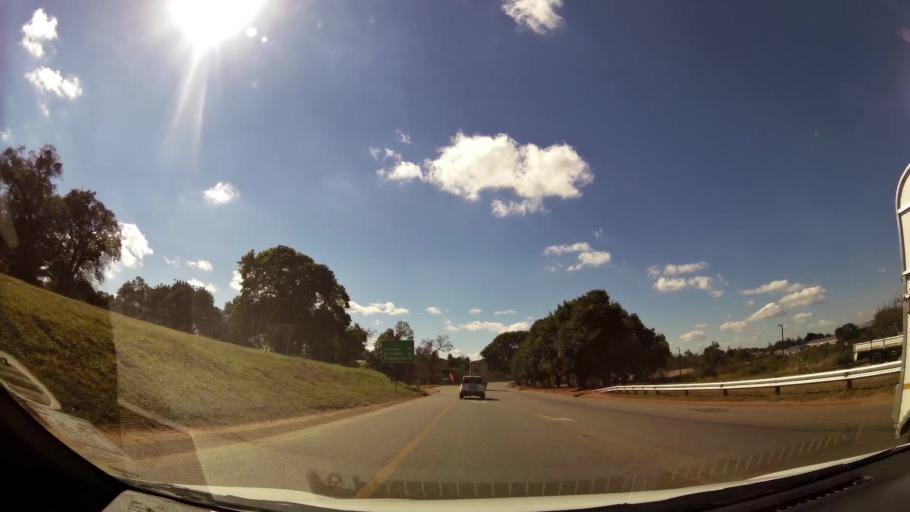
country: ZA
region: Limpopo
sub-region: Mopani District Municipality
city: Tzaneen
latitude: -23.8220
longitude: 30.1606
